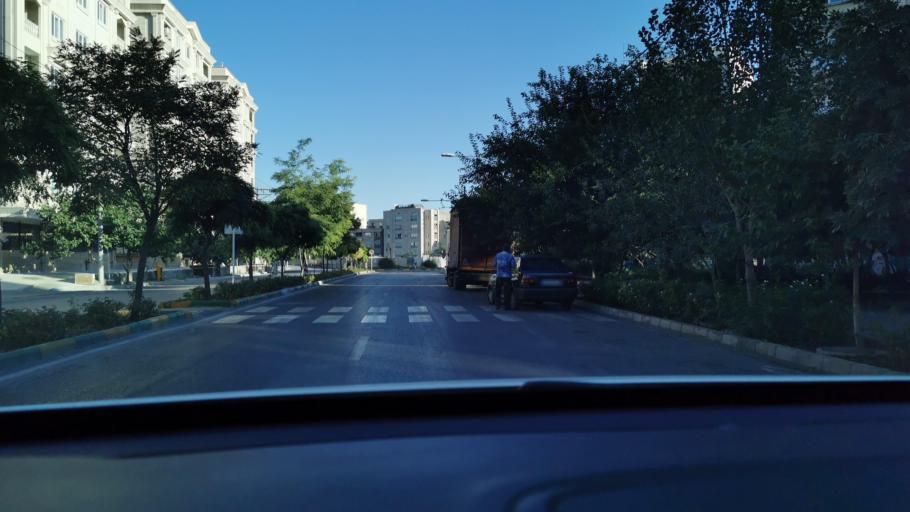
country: IR
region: Razavi Khorasan
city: Mashhad
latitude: 36.3596
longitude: 59.4842
